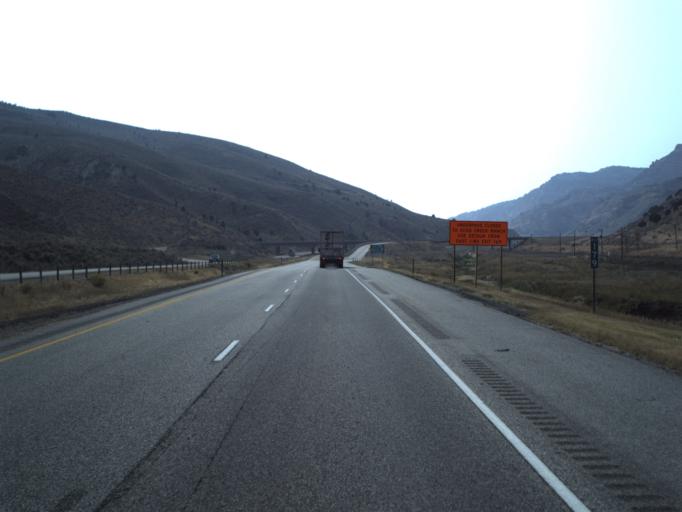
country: US
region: Utah
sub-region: Summit County
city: Coalville
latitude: 41.0707
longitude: -111.2638
